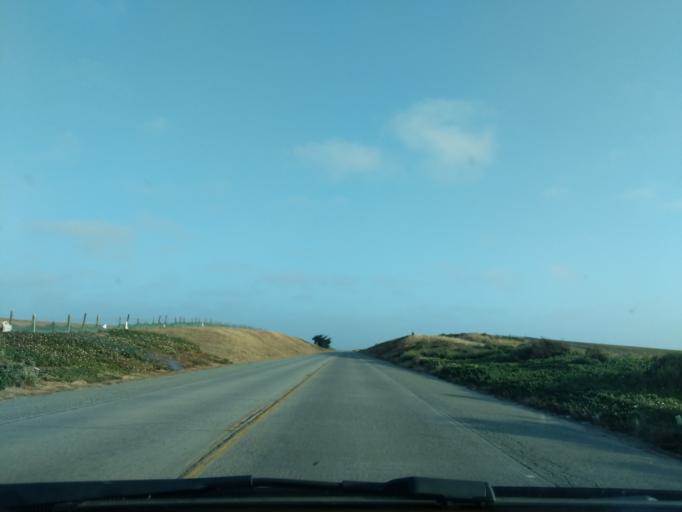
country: US
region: California
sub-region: Monterey County
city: Marina
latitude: 36.7192
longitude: -121.7878
